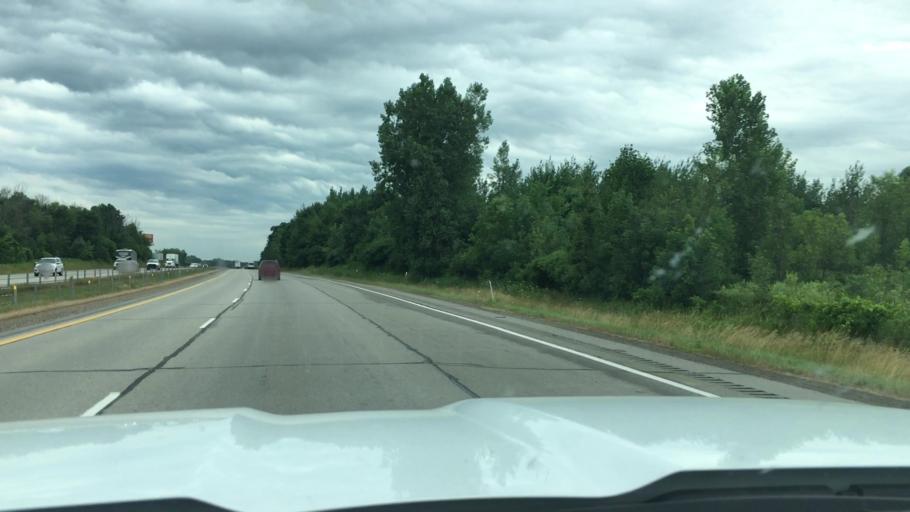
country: US
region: Michigan
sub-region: Allegan County
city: Wayland
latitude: 42.7219
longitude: -85.6709
